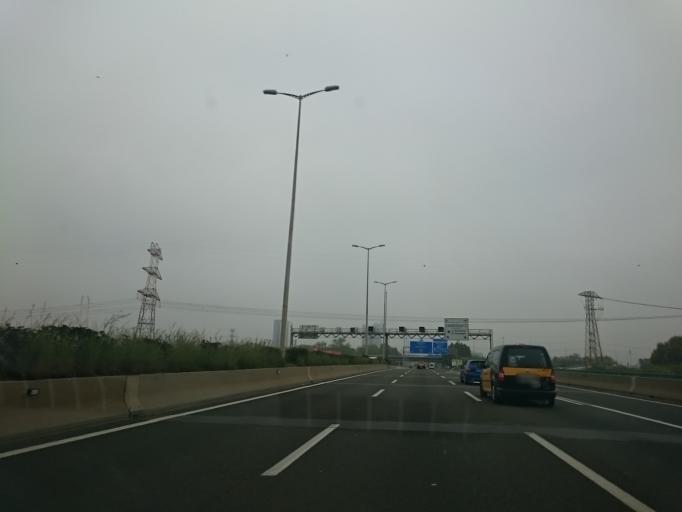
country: ES
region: Catalonia
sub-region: Provincia de Barcelona
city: El Prat de Llobregat
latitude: 41.3370
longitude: 2.0985
